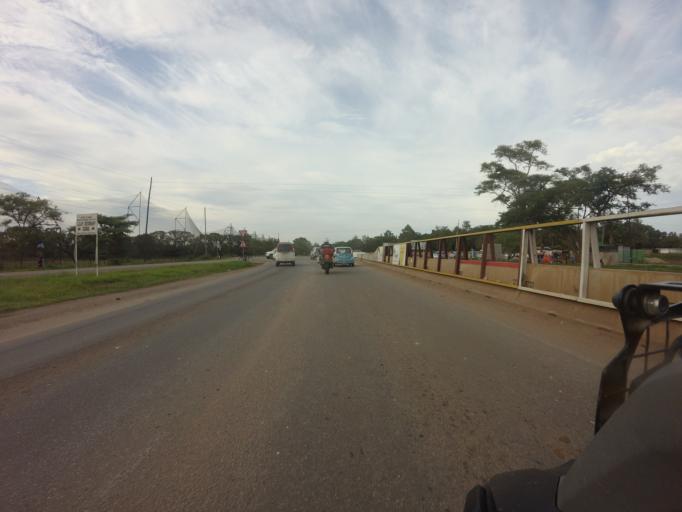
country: ZM
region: Lusaka
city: Lusaka
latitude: -15.5161
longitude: 28.2625
